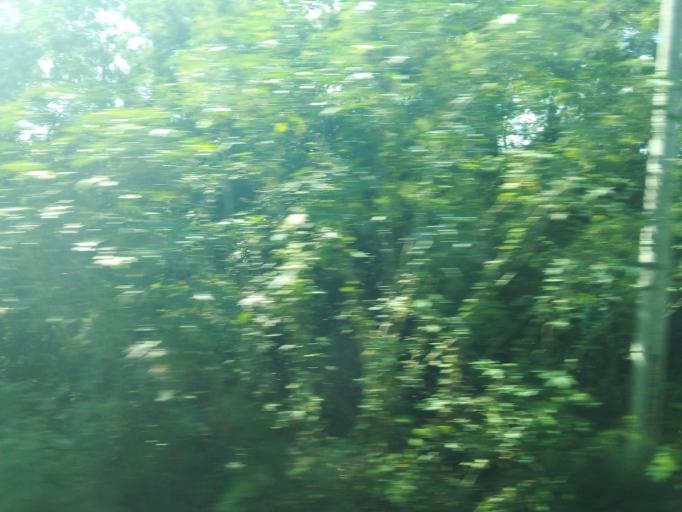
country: BR
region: Minas Gerais
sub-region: Governador Valadares
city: Governador Valadares
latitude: -18.8717
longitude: -41.7788
